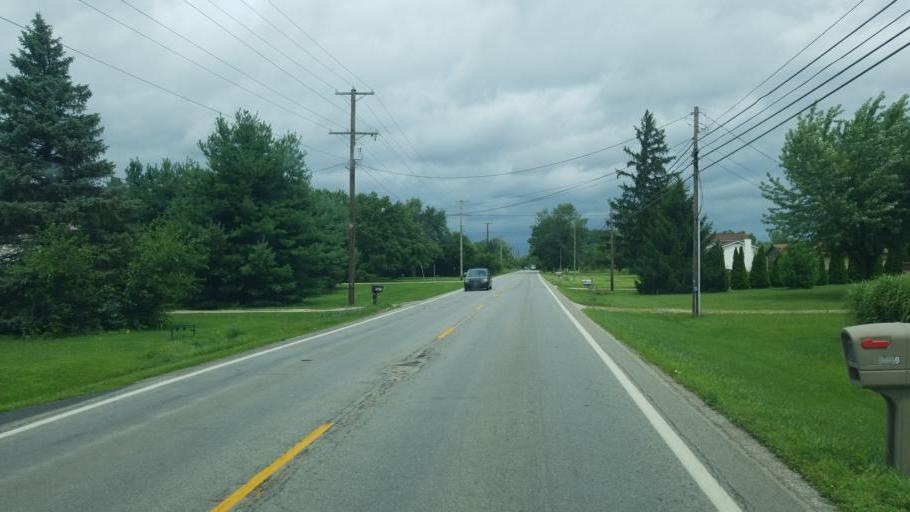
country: US
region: Ohio
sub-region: Franklin County
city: Grove City
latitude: 39.8587
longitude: -83.0278
